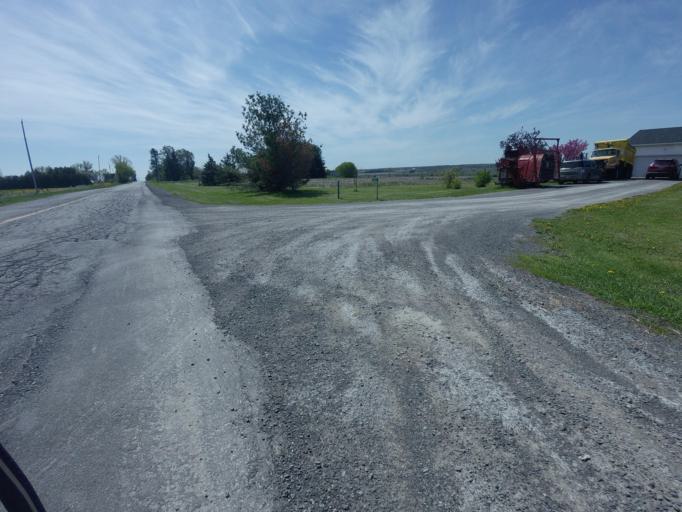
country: CA
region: Ontario
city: Arnprior
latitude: 45.3857
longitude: -76.1339
